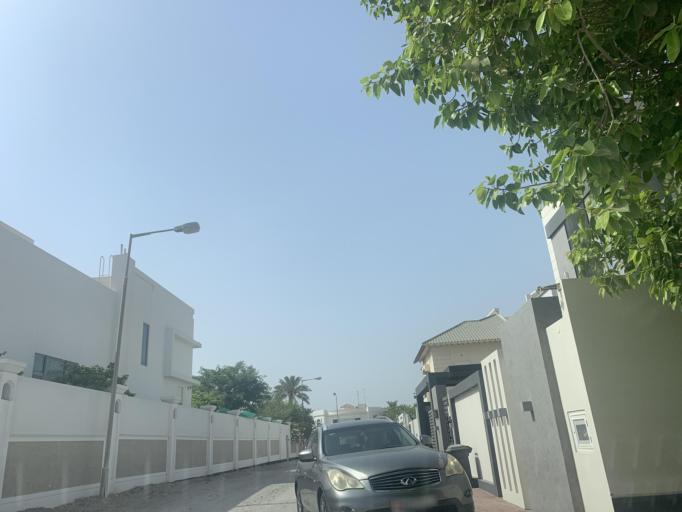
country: BH
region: Northern
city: Madinat `Isa
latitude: 26.1945
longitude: 50.5003
